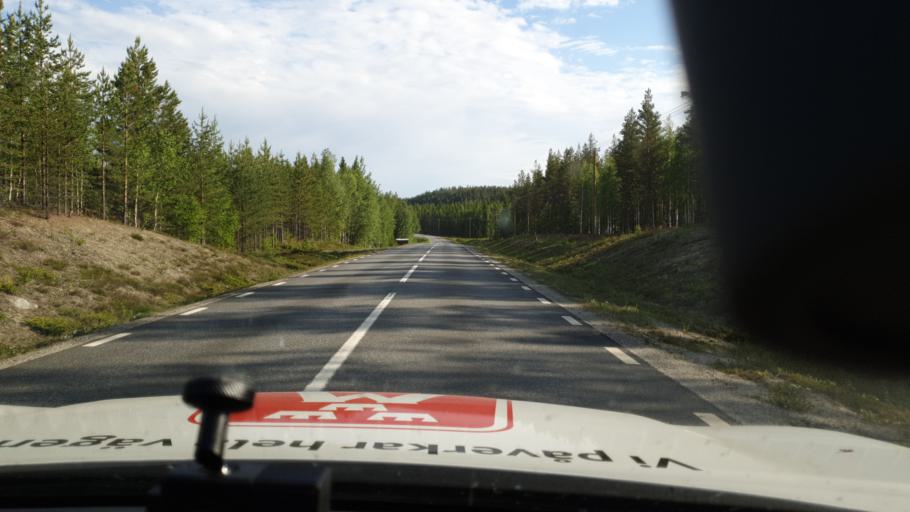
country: SE
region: Vaesterbotten
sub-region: Bjurholms Kommun
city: Bjurholm
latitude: 64.3632
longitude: 19.1398
